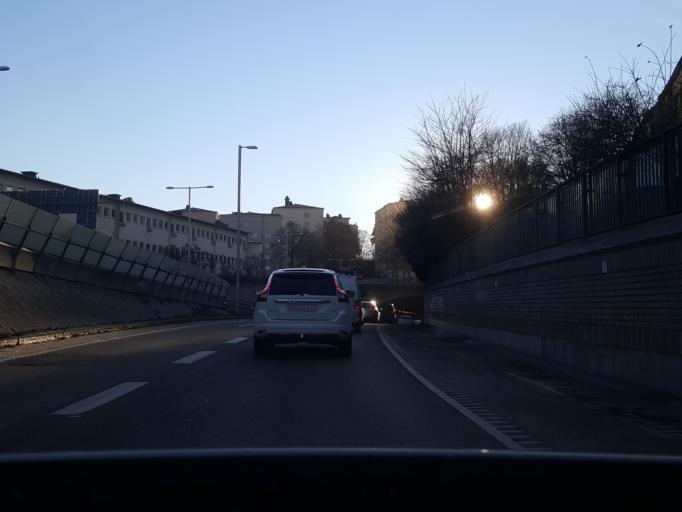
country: SE
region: Stockholm
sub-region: Solna Kommun
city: Solna
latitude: 59.3305
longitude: 18.0096
